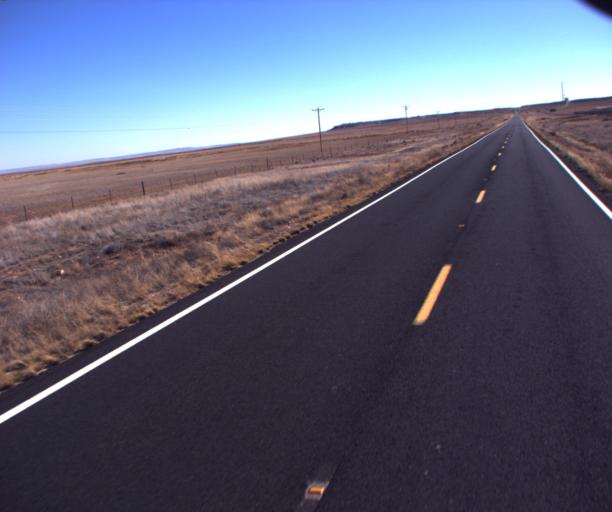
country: US
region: Arizona
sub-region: Coconino County
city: Tuba City
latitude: 36.0026
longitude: -111.0420
